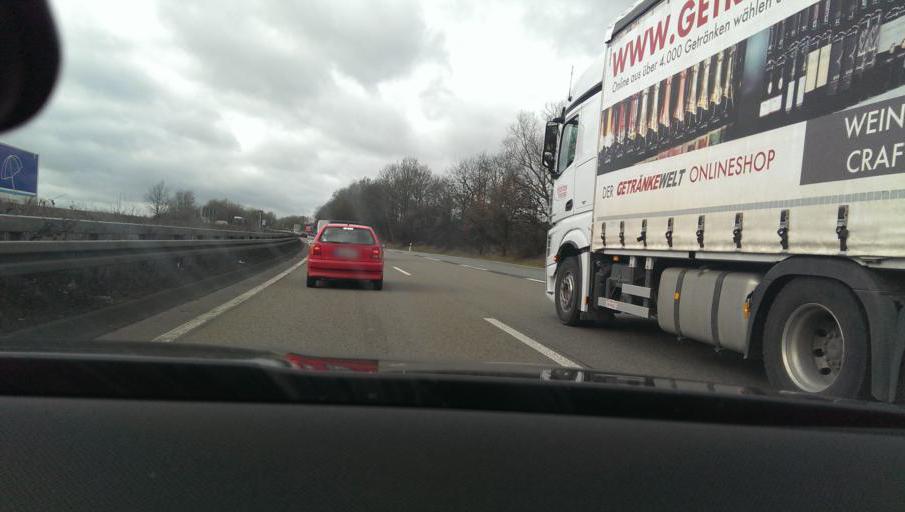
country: DE
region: Hesse
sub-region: Regierungsbezirk Kassel
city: Niederaula
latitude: 50.7779
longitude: 9.5808
